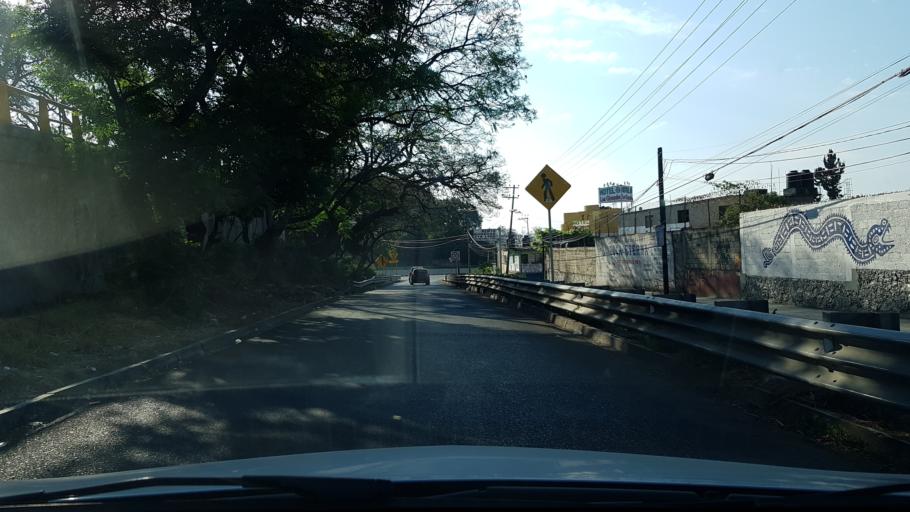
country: MX
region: Morelos
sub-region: Cuernavaca
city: Fraccionamiento Lomas de Ahuatlan
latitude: 18.9672
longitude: -99.2374
